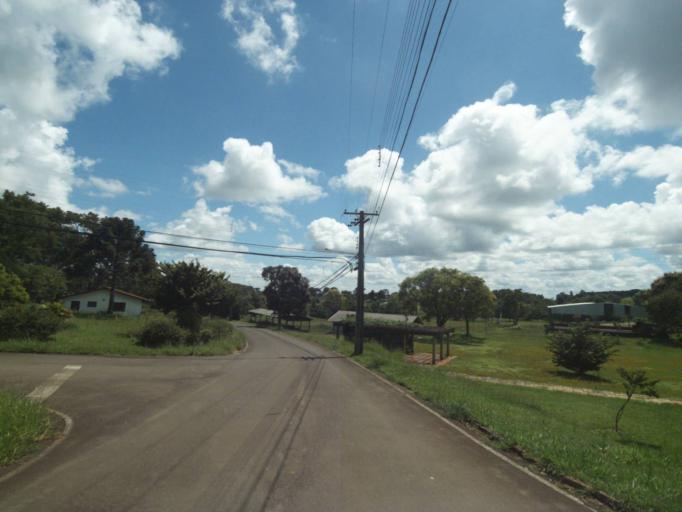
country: BR
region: Parana
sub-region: Pinhao
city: Pinhao
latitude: -25.7937
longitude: -52.0879
